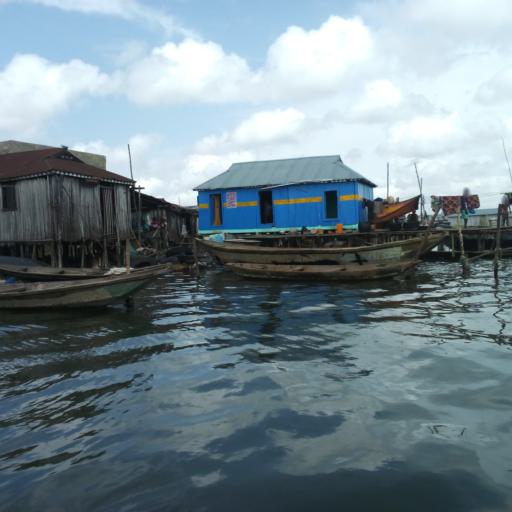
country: BJ
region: Littoral
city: Cotonou
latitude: 6.3926
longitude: 2.4338
